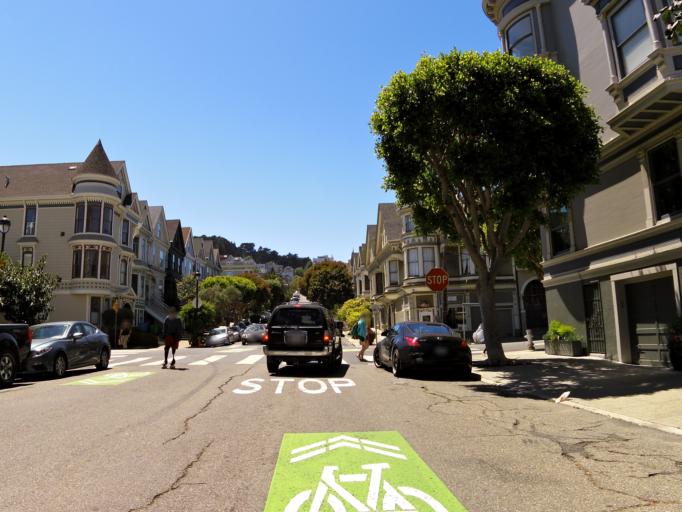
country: US
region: California
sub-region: San Francisco County
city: San Francisco
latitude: 37.7709
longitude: -122.4332
